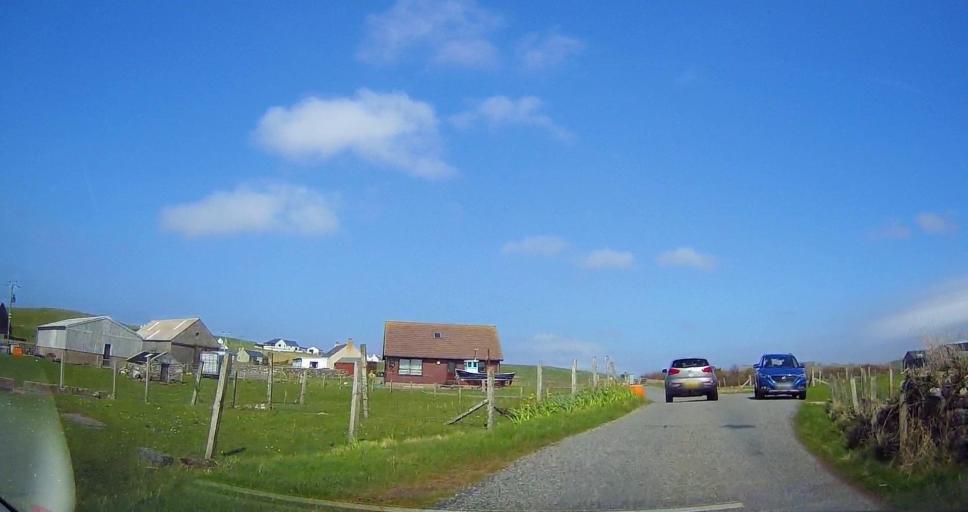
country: GB
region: Scotland
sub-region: Shetland Islands
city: Sandwick
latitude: 60.0658
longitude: -1.3376
